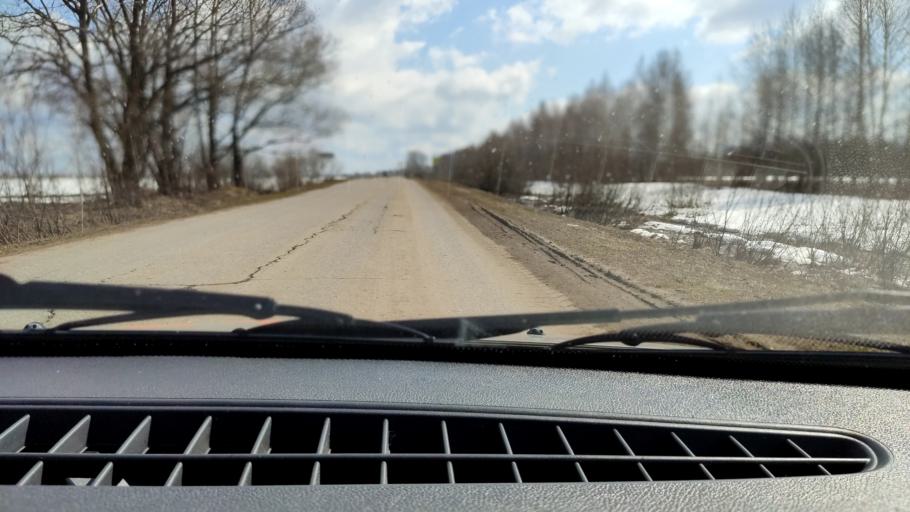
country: RU
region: Bashkortostan
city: Kudeyevskiy
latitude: 54.8650
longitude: 56.7474
